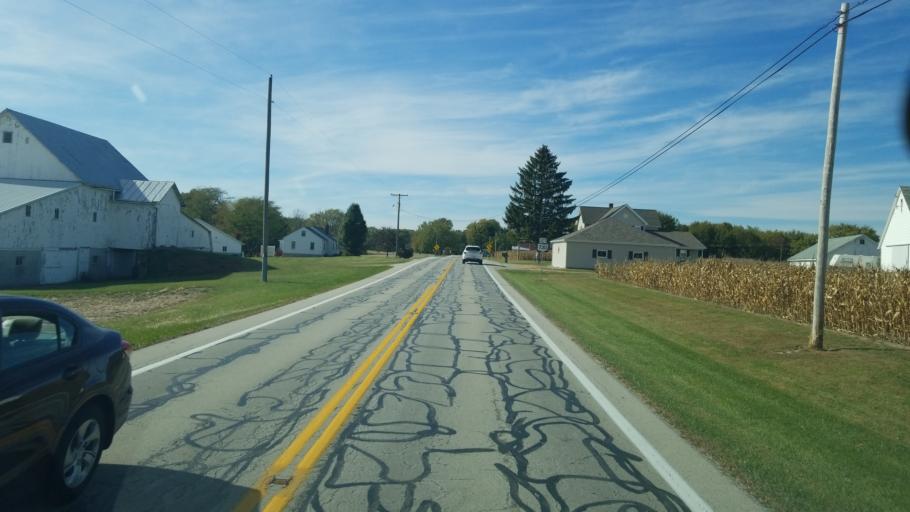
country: US
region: Ohio
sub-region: Clinton County
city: Blanchester
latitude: 39.3796
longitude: -83.9249
